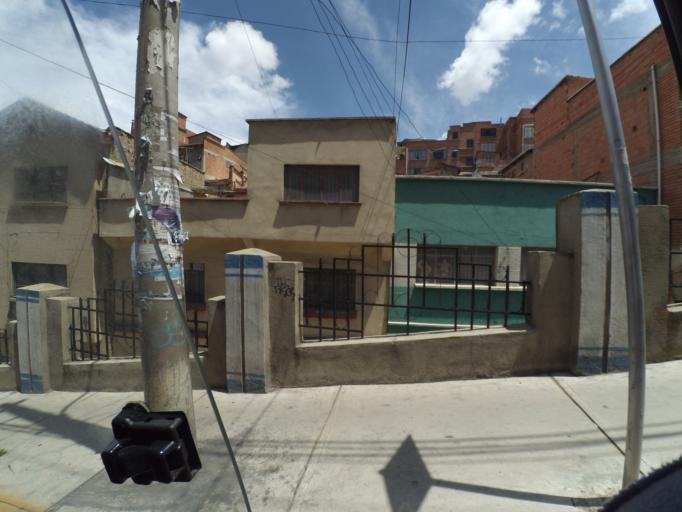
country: BO
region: La Paz
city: La Paz
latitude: -16.4944
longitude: -68.1300
